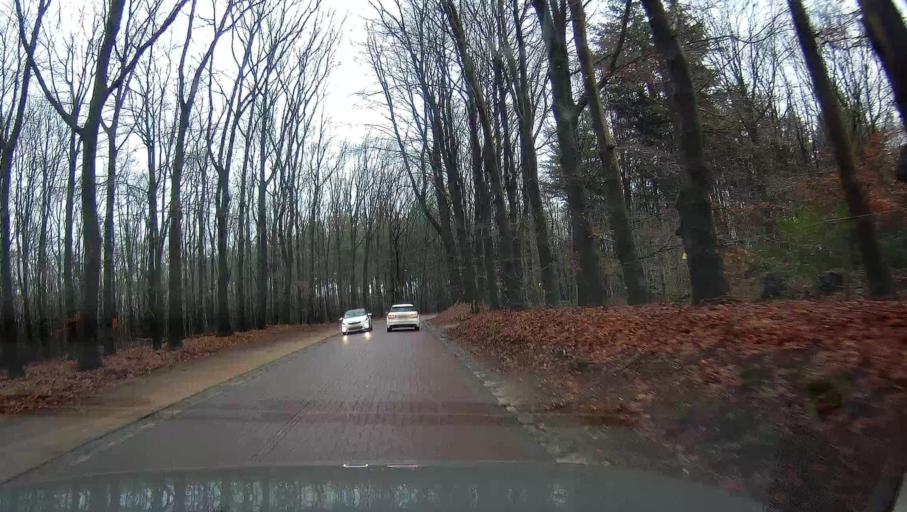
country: NL
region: Gelderland
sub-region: Gemeente Apeldoorn
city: Uddel
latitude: 52.1946
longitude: 5.8435
